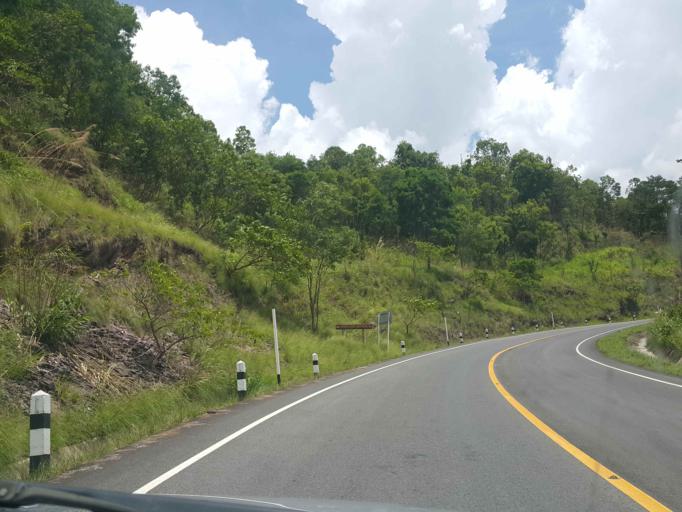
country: TH
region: Phayao
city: Chiang Muan
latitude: 18.8401
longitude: 100.3528
